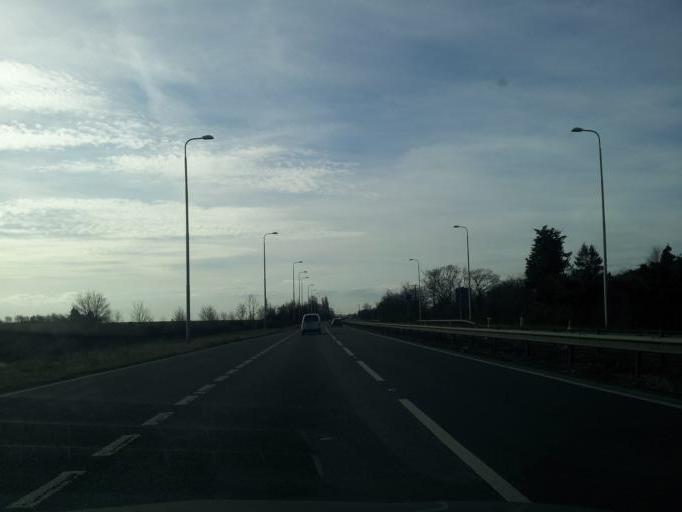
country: GB
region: England
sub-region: Central Bedfordshire
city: Tempsford
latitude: 52.1549
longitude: -0.3011
